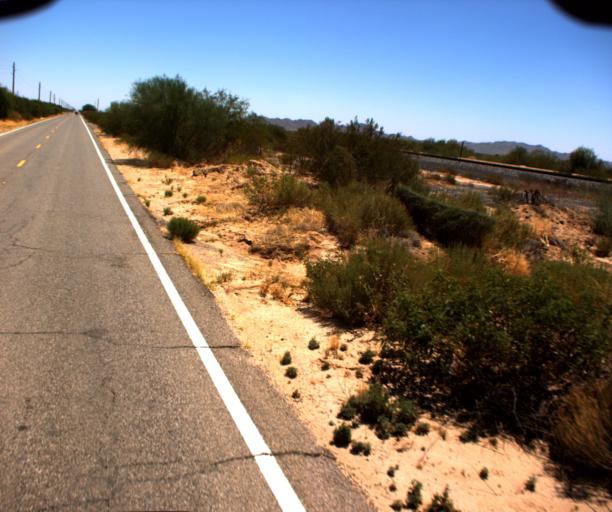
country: US
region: Arizona
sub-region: Pinal County
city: Maricopa
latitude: 33.0586
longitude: -112.2593
